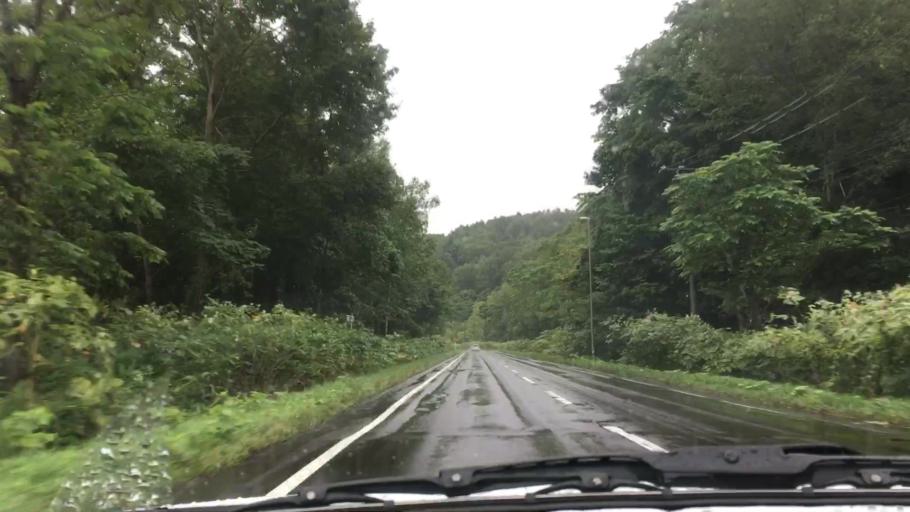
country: JP
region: Hokkaido
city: Niseko Town
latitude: 42.8224
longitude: 141.0030
